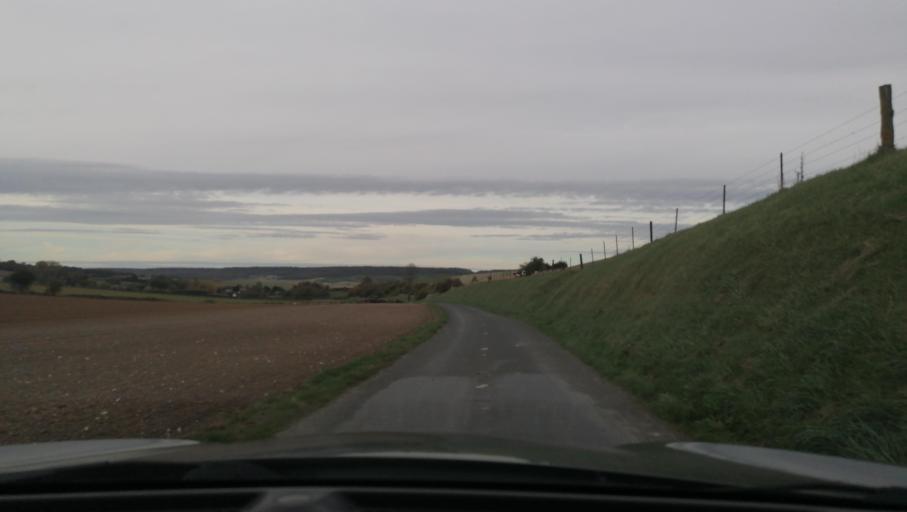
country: FR
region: Picardie
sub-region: Departement de la Somme
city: Bouttencourt
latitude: 49.8965
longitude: 1.6744
